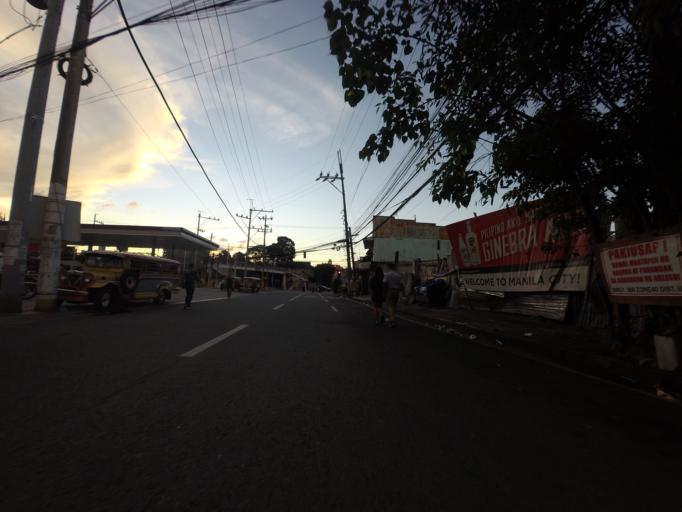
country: PH
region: Metro Manila
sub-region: City of Manila
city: Quiapo
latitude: 14.5965
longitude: 120.9902
